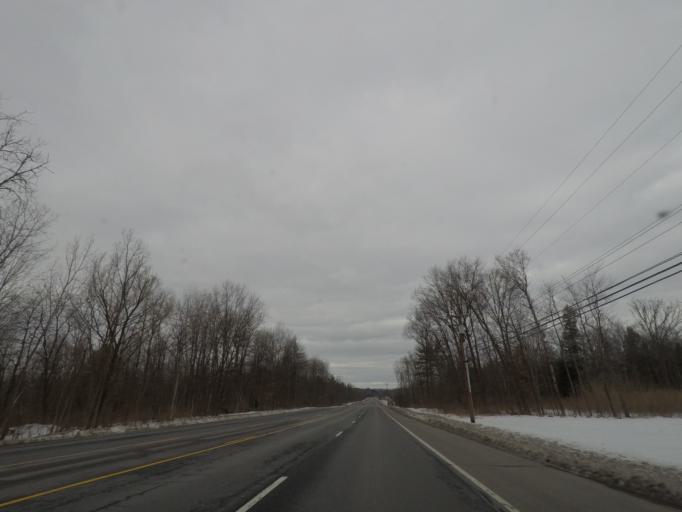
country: US
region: New York
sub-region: Saratoga County
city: Country Knolls
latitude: 42.9076
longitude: -73.7823
